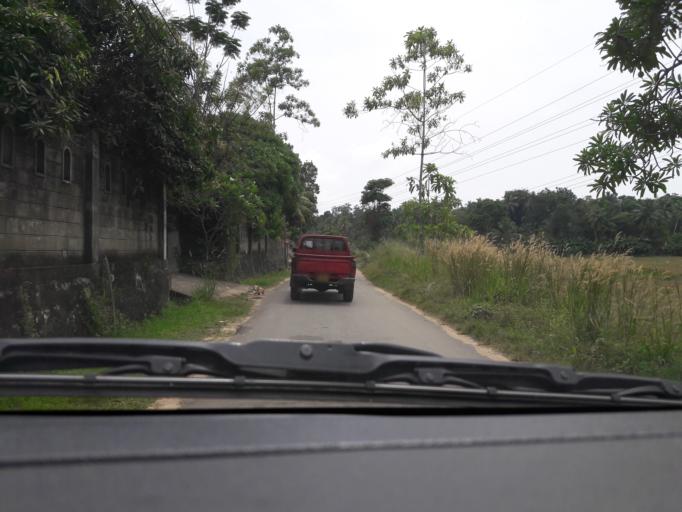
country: LK
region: Southern
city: Unawatuna
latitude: 6.0547
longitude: 80.2492
